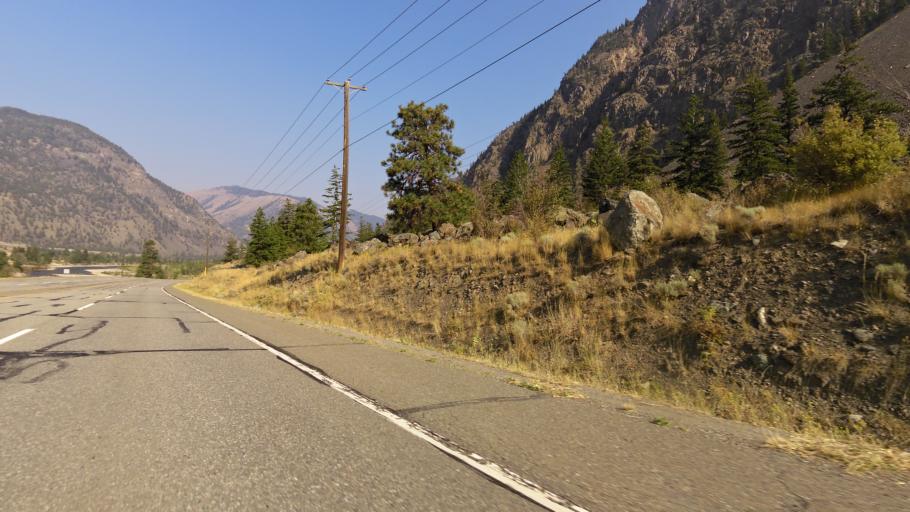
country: CA
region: British Columbia
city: Oliver
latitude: 49.2299
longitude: -119.9765
